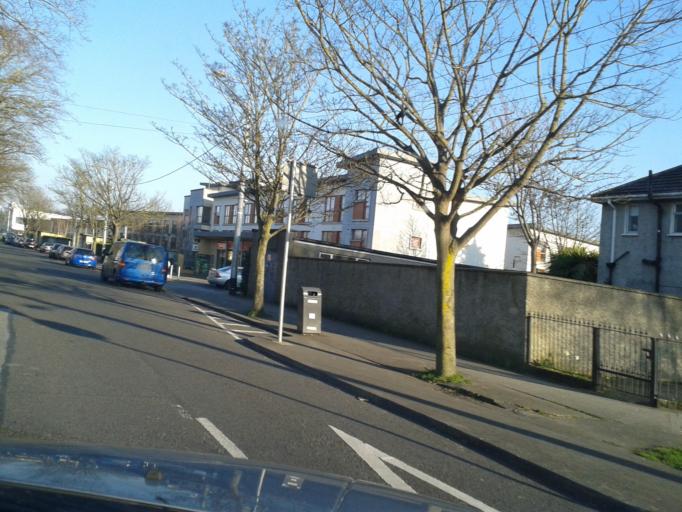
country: IE
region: Leinster
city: Glasnevin
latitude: 53.3891
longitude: -6.2576
